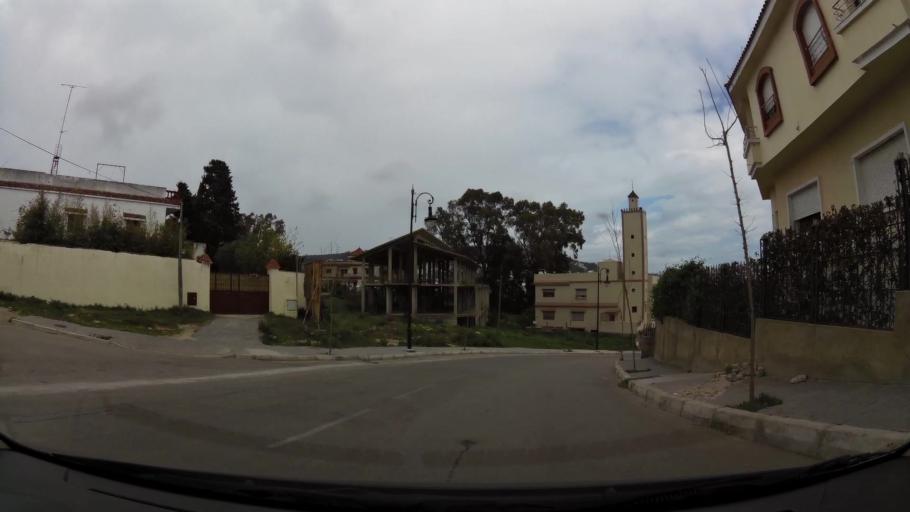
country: MA
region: Tanger-Tetouan
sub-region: Tanger-Assilah
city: Boukhalef
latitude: 35.7696
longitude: -5.8623
